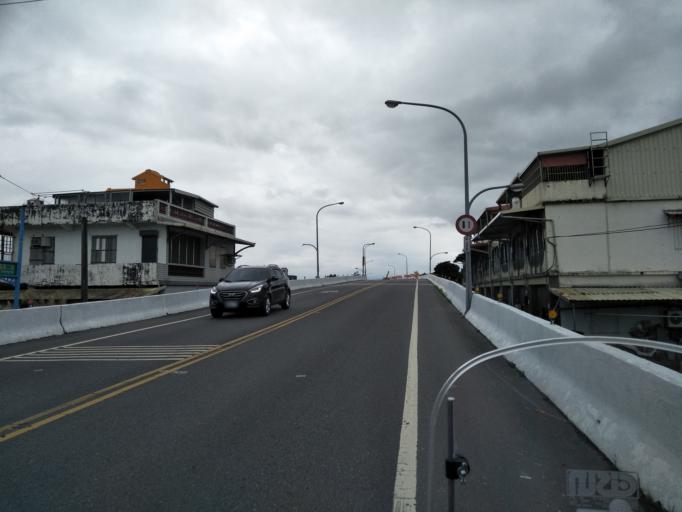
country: TW
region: Taiwan
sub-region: Yilan
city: Yilan
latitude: 24.8102
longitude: 121.7918
